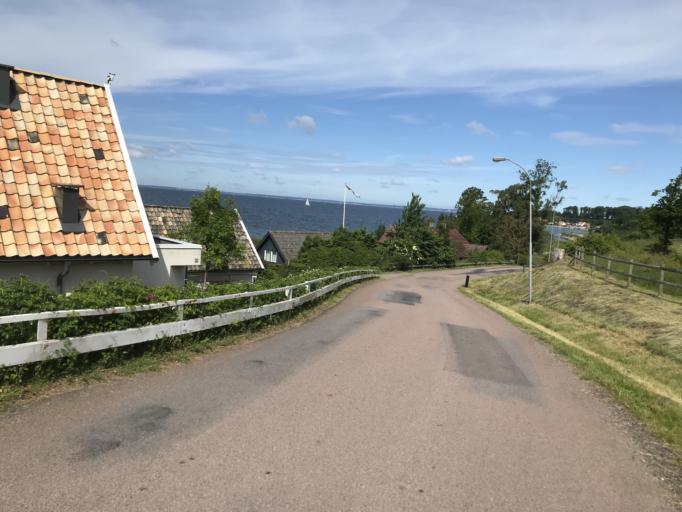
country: SE
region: Skane
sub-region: Helsingborg
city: Glumslov
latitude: 55.9322
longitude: 12.7899
